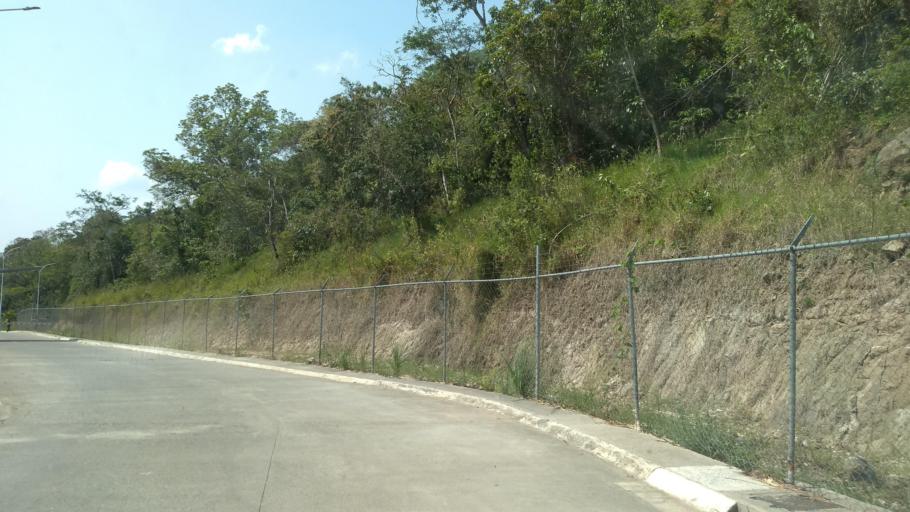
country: MX
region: Veracruz
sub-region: Emiliano Zapata
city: Las Trancas
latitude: 19.5245
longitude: -96.8637
